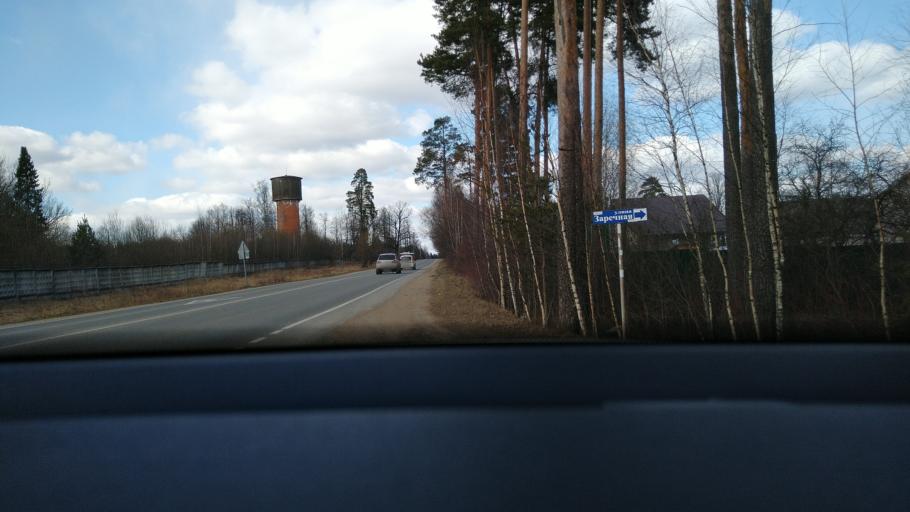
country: RU
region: Moskovskaya
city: Zvenigorod
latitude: 55.6490
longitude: 36.8216
